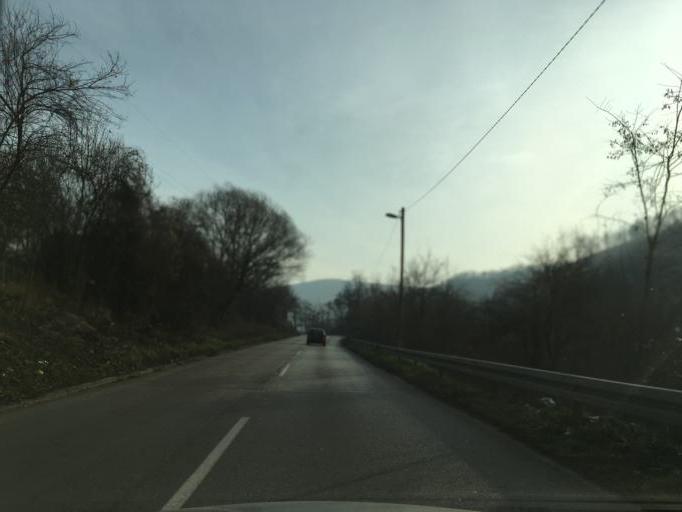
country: BA
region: Federation of Bosnia and Herzegovina
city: Zenica
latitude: 44.1934
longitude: 17.8812
